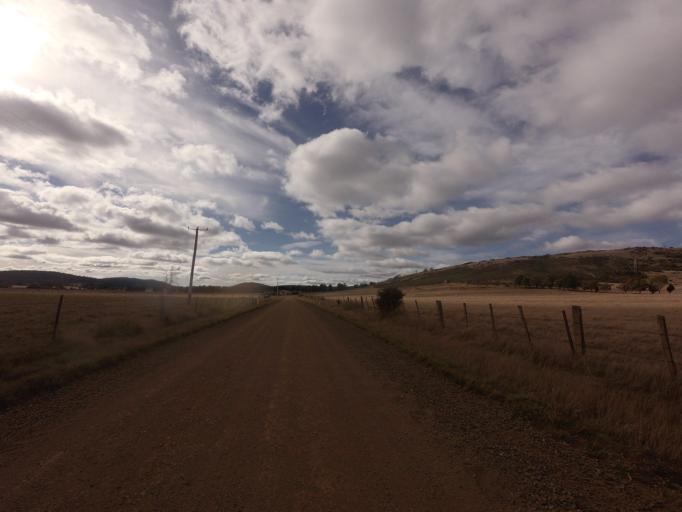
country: AU
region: Tasmania
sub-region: Brighton
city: Bridgewater
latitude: -42.4199
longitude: 147.3928
